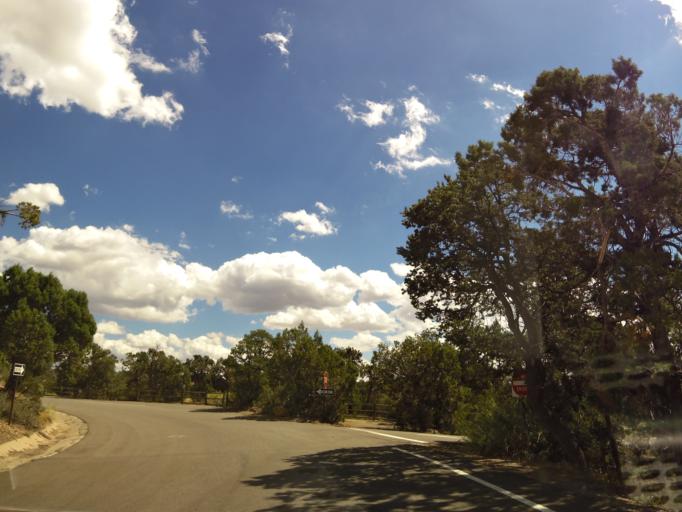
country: US
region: Colorado
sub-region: Montezuma County
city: Cortez
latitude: 37.1832
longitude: -108.4899
